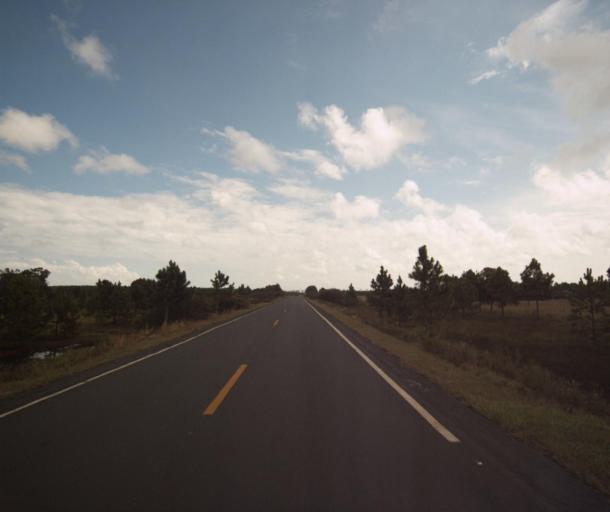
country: BR
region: Rio Grande do Sul
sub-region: Sao Lourenco Do Sul
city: Sao Lourenco do Sul
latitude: -31.4361
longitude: -51.1945
